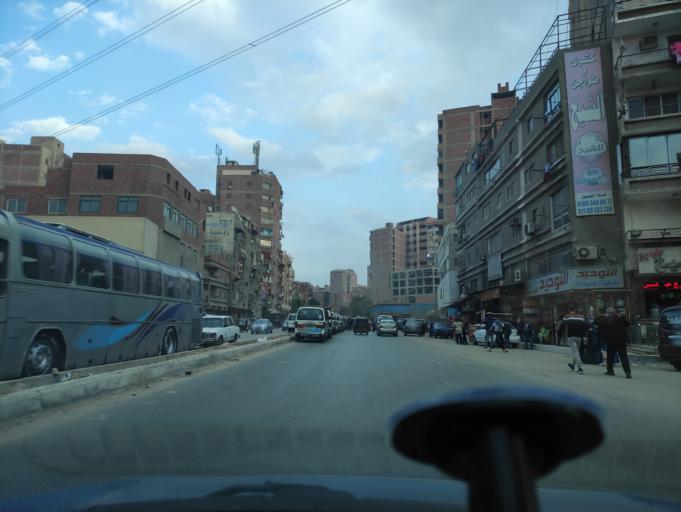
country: EG
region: Muhafazat al Qalyubiyah
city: Al Khankah
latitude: 30.1328
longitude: 31.3595
